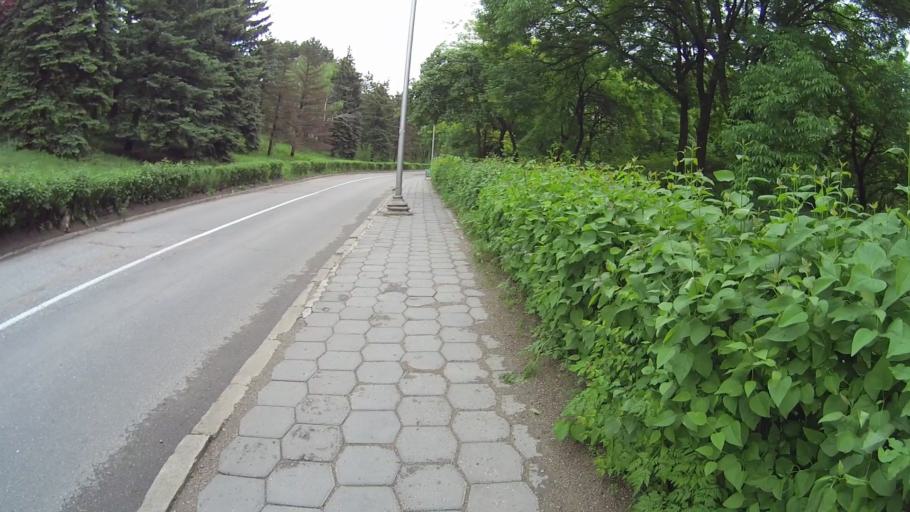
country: RU
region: Stavropol'skiy
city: Goryachevodskiy
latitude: 44.0421
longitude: 43.0838
